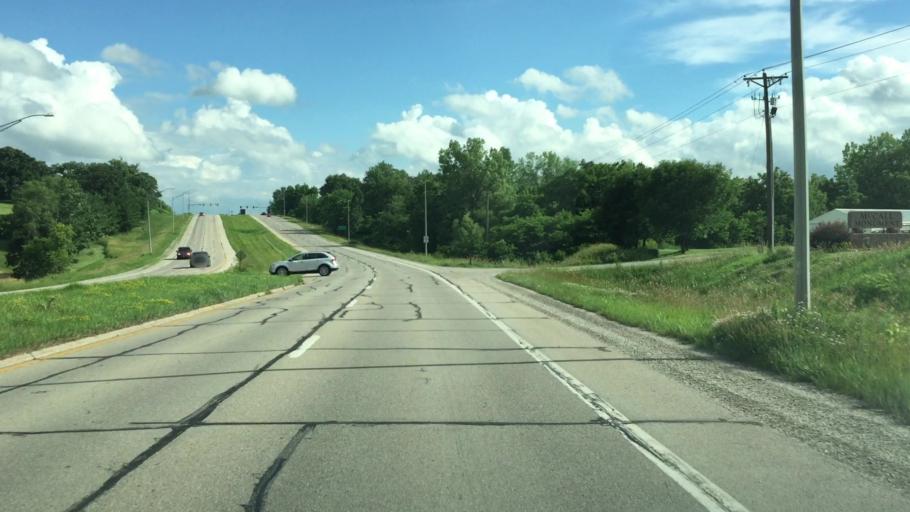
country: US
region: Iowa
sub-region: Jasper County
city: Newton
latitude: 41.6932
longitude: -93.0773
